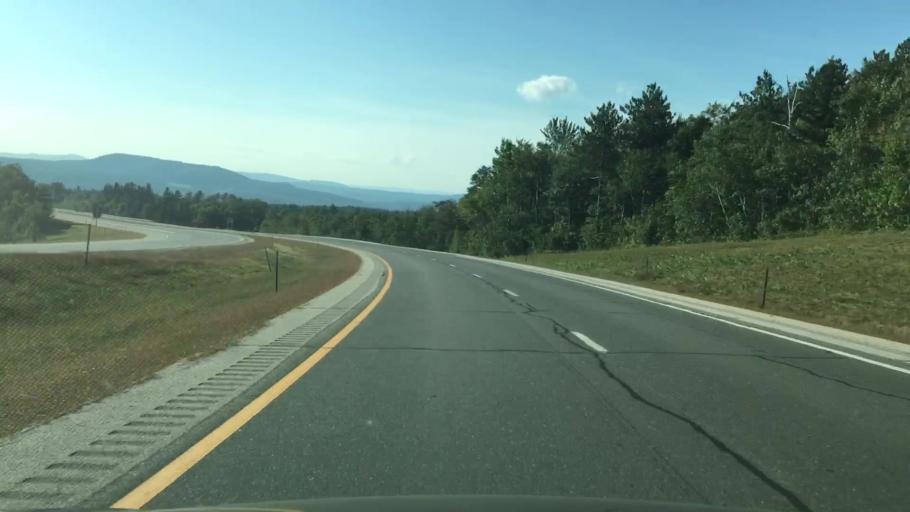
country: US
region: New Hampshire
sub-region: Grafton County
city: Deerfield
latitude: 44.2012
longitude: -71.6837
